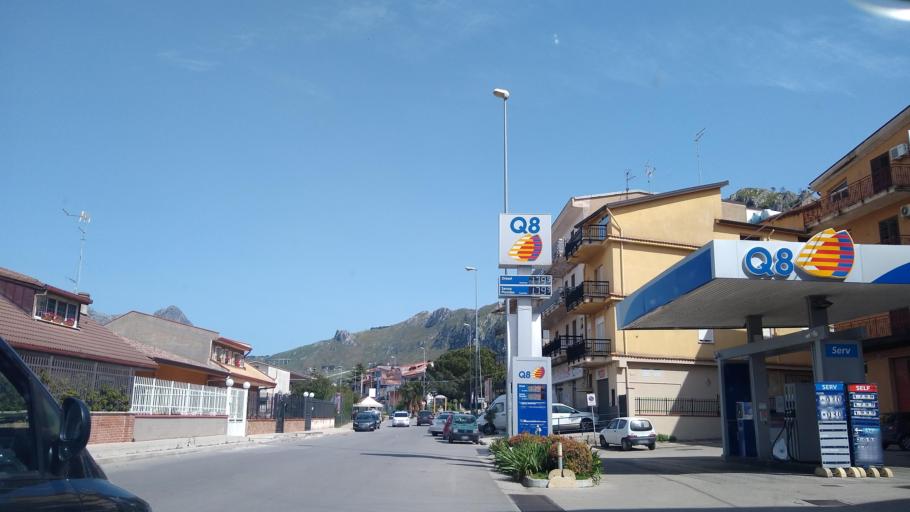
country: IT
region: Sicily
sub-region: Palermo
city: San Giuseppe Jato
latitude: 37.9752
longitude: 13.1927
